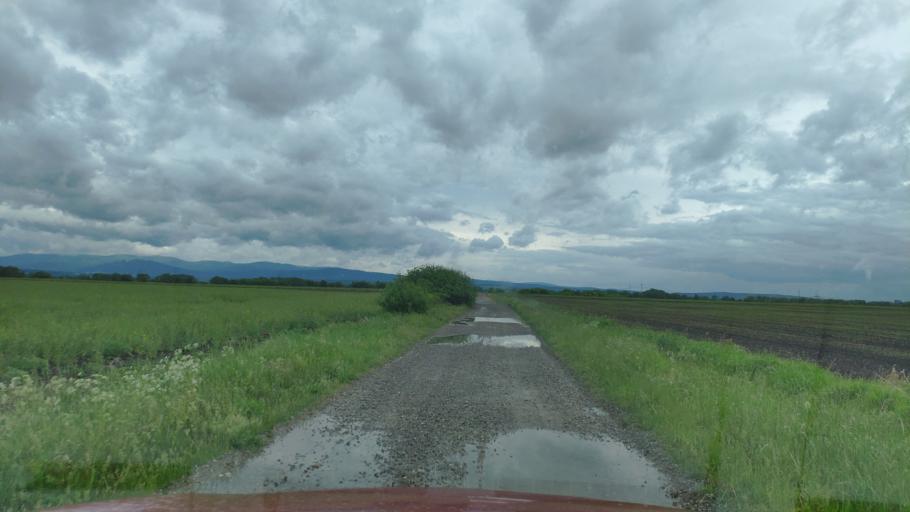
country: SK
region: Kosicky
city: Moldava nad Bodvou
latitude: 48.5485
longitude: 21.1133
